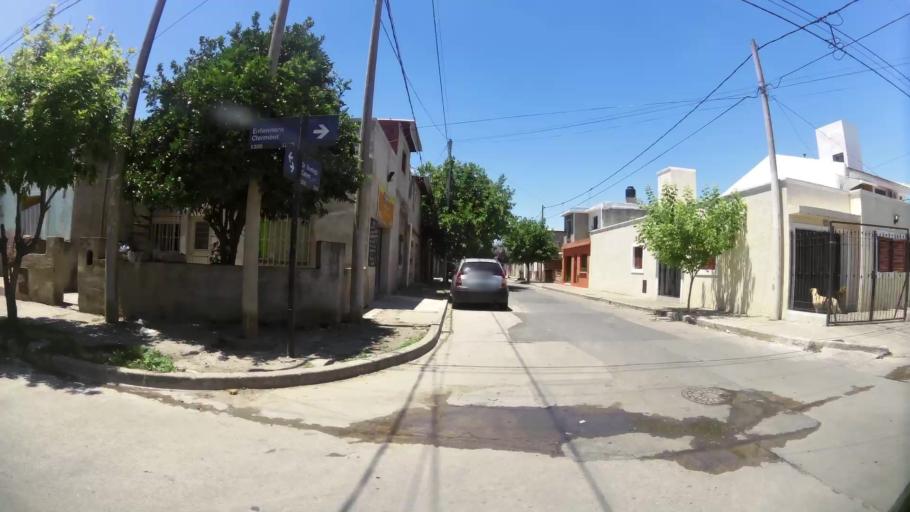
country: AR
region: Cordoba
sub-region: Departamento de Capital
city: Cordoba
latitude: -31.3944
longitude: -64.2069
